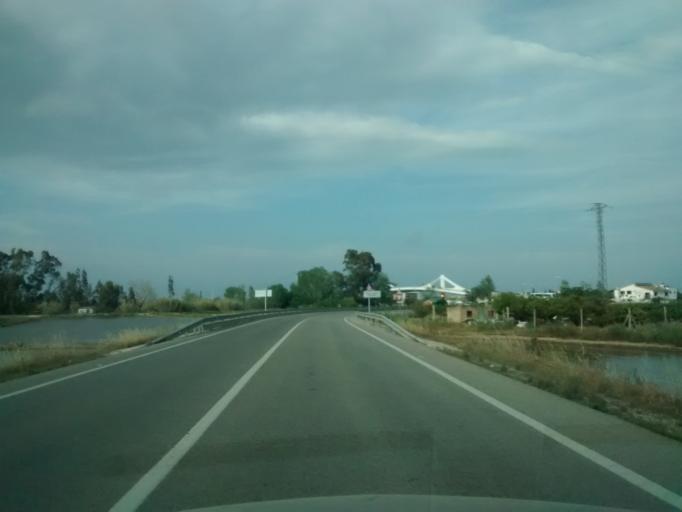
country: ES
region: Catalonia
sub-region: Provincia de Tarragona
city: Deltebre
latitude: 40.7099
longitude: 0.7144
